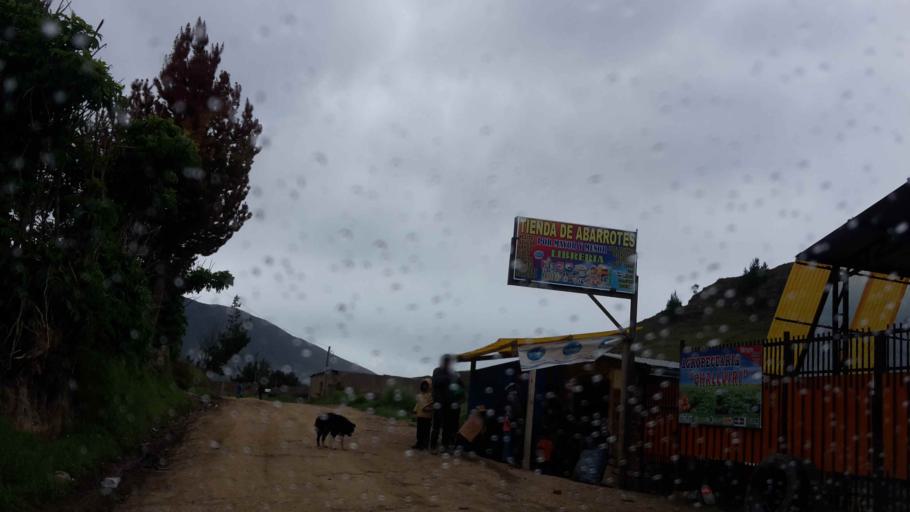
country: BO
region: Cochabamba
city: Cochabamba
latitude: -17.1327
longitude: -66.1058
